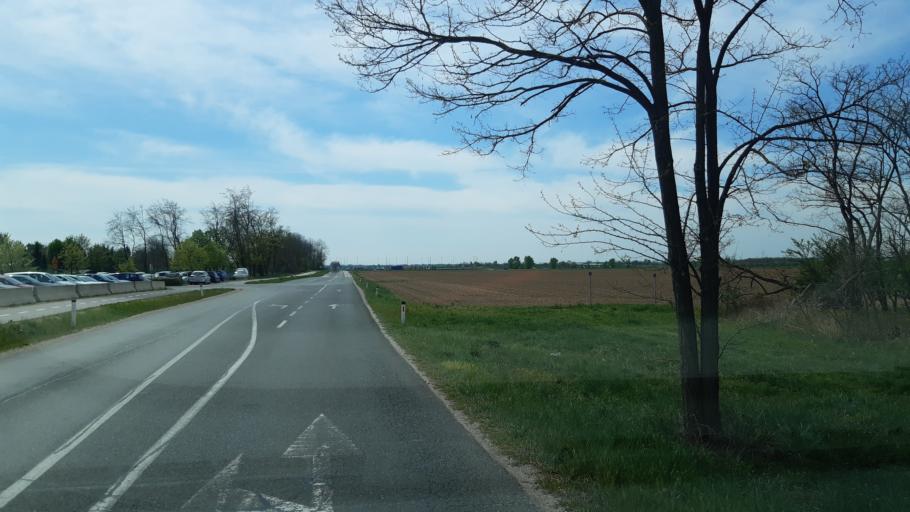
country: SI
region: Murska Sobota
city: Murska Sobota
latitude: 46.6426
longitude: 16.1659
